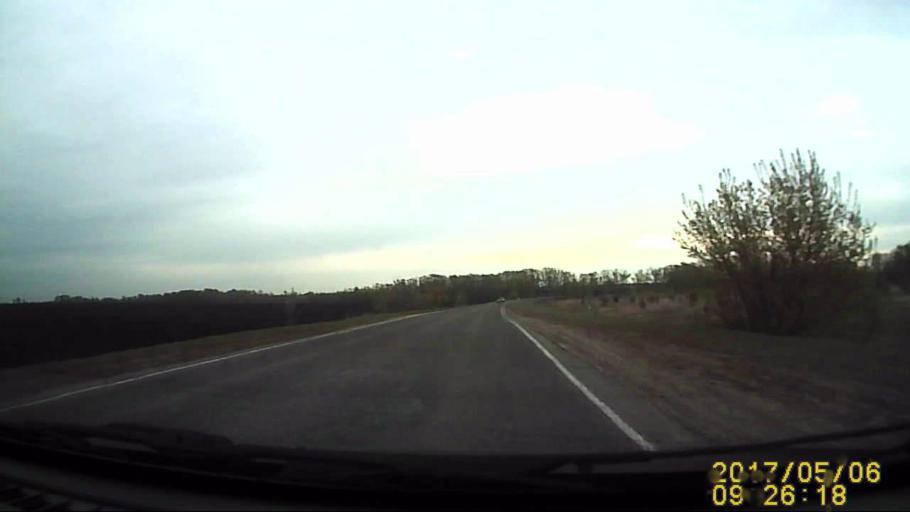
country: RU
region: Ulyanovsk
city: Cherdakly
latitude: 54.3851
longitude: 48.8341
